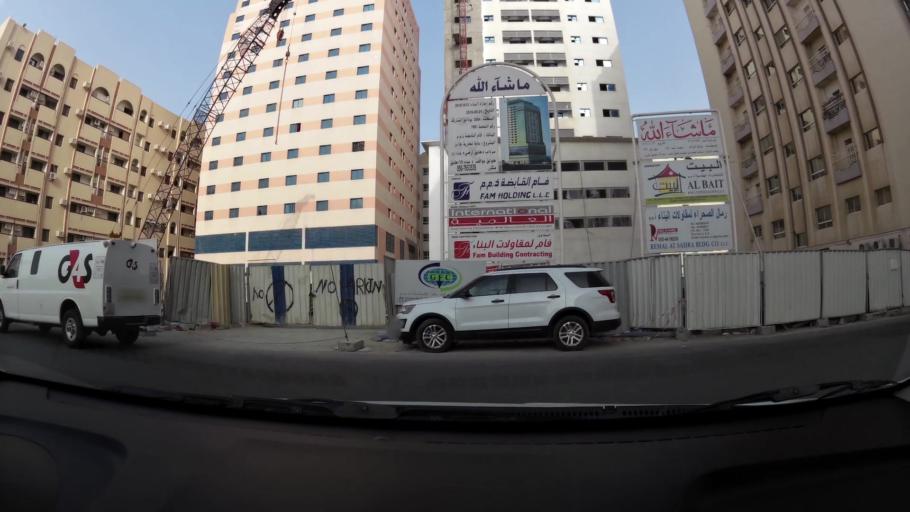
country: AE
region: Ash Shariqah
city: Sharjah
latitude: 25.3431
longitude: 55.3990
